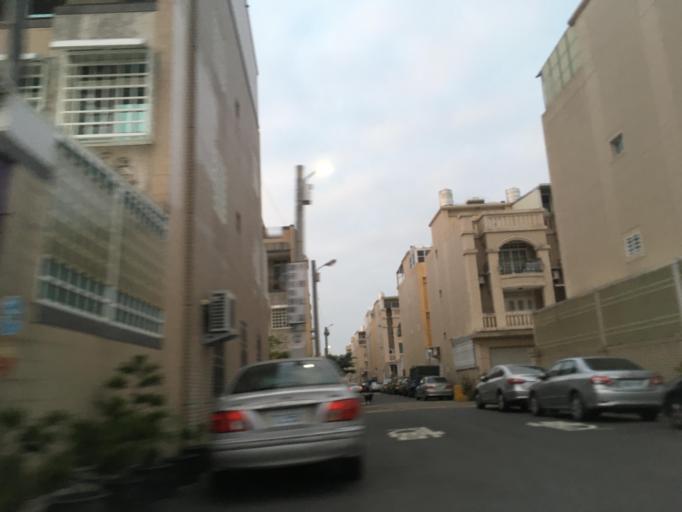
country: TW
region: Taiwan
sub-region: Yunlin
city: Douliu
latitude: 23.7032
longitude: 120.4470
